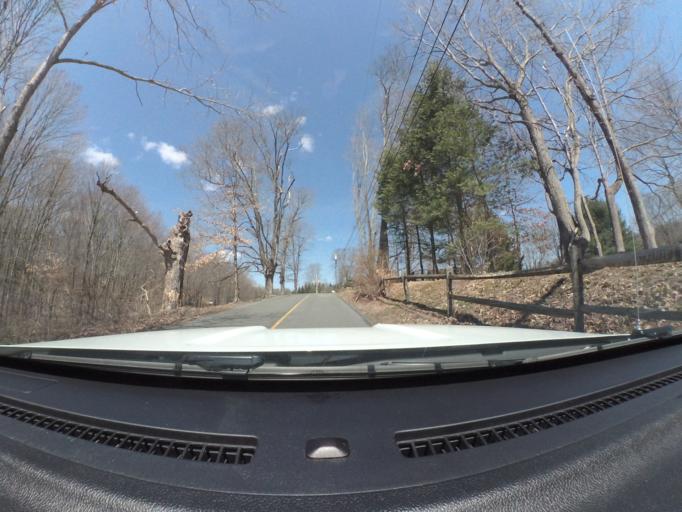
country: US
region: Connecticut
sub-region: Litchfield County
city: Bethlehem Village
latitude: 41.6142
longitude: -73.1724
